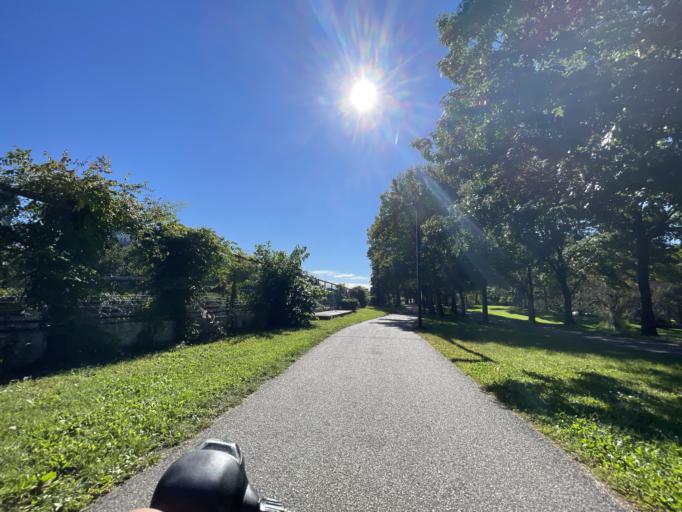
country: US
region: Massachusetts
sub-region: Suffolk County
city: Jamaica Plain
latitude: 42.3037
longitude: -71.1121
